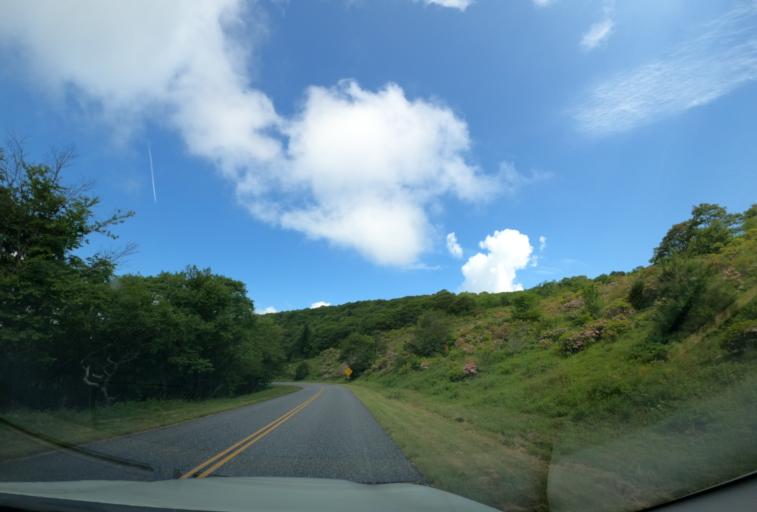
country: US
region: North Carolina
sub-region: Haywood County
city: Hazelwood
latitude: 35.3811
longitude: -83.0268
